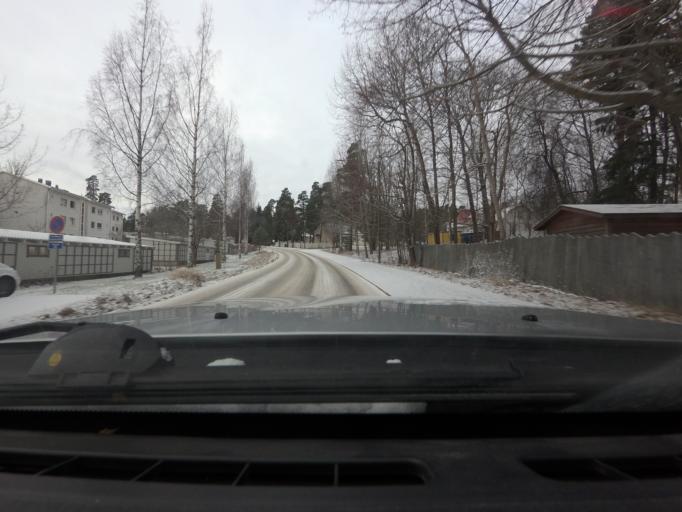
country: FI
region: Uusimaa
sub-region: Helsinki
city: Kilo
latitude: 60.2194
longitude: 24.7782
